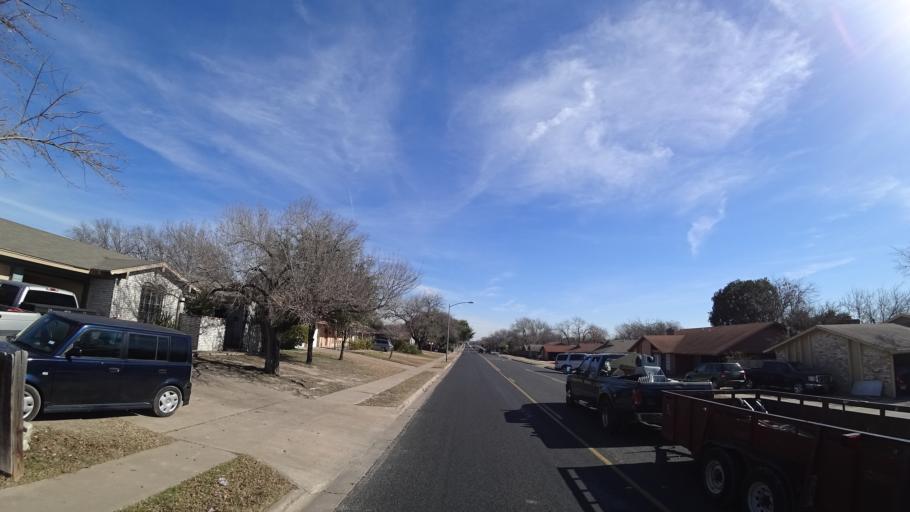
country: US
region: Texas
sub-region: Travis County
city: Wells Branch
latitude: 30.3719
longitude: -97.7108
